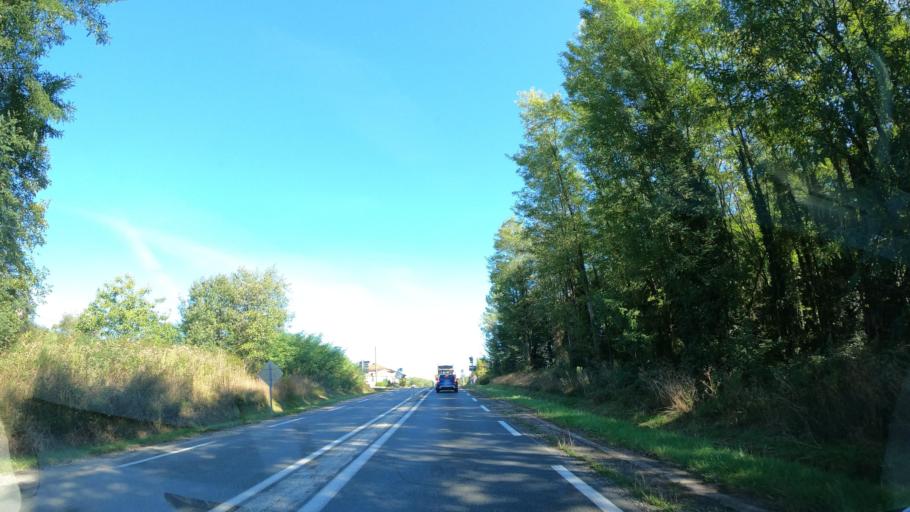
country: FR
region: Aquitaine
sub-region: Departement de la Dordogne
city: Notre-Dame-de-Sanilhac
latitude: 45.0927
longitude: 0.6929
